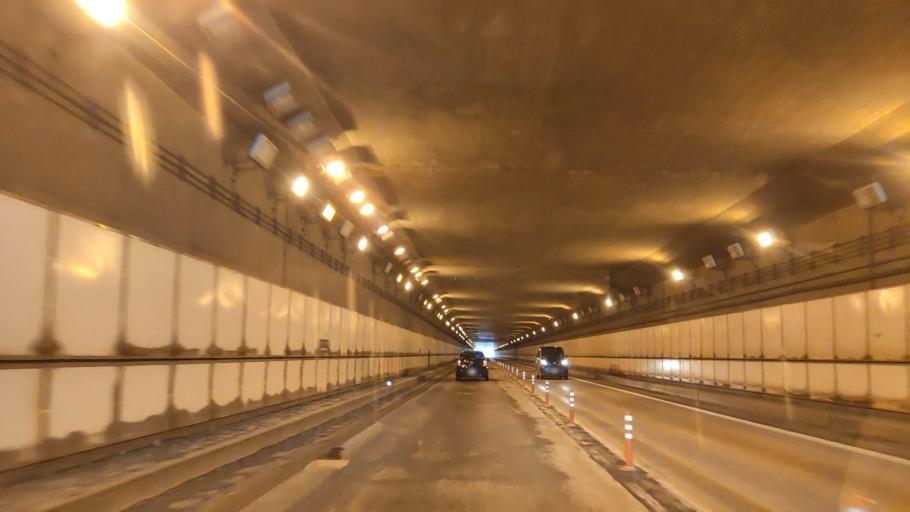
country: JP
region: Akita
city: Odate
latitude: 40.2766
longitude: 140.5352
